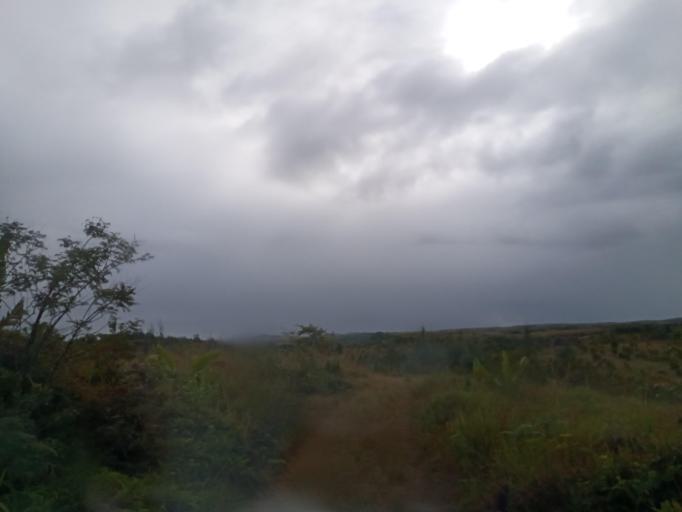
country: MG
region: Atsimo-Atsinanana
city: Vohipaho
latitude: -24.0007
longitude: 47.4043
